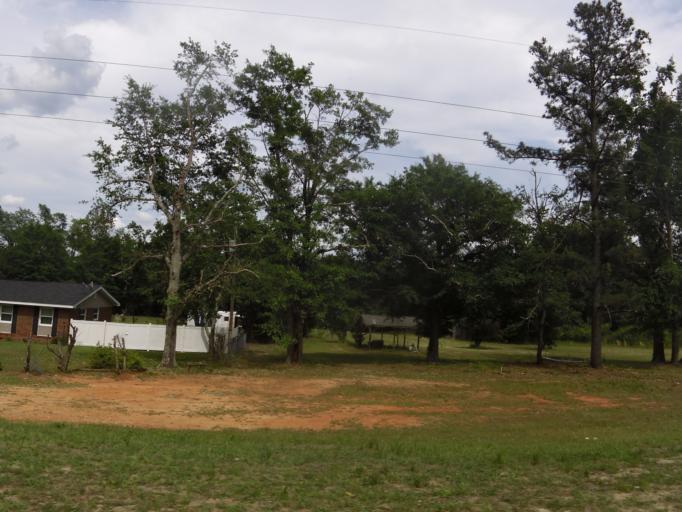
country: US
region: Georgia
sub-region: Jefferson County
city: Louisville
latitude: 33.0941
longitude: -82.4055
